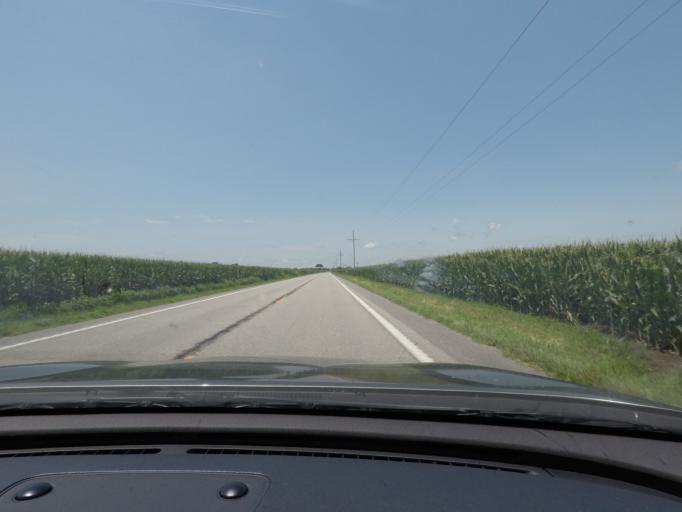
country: US
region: Missouri
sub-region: Saline County
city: Marshall
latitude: 39.1920
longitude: -93.3300
